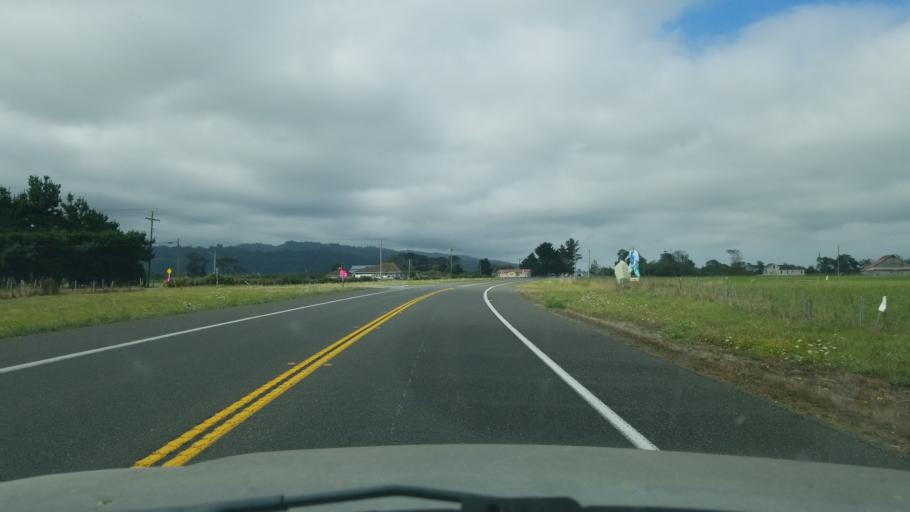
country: US
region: California
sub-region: Humboldt County
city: Ferndale
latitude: 40.5962
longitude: -124.2346
